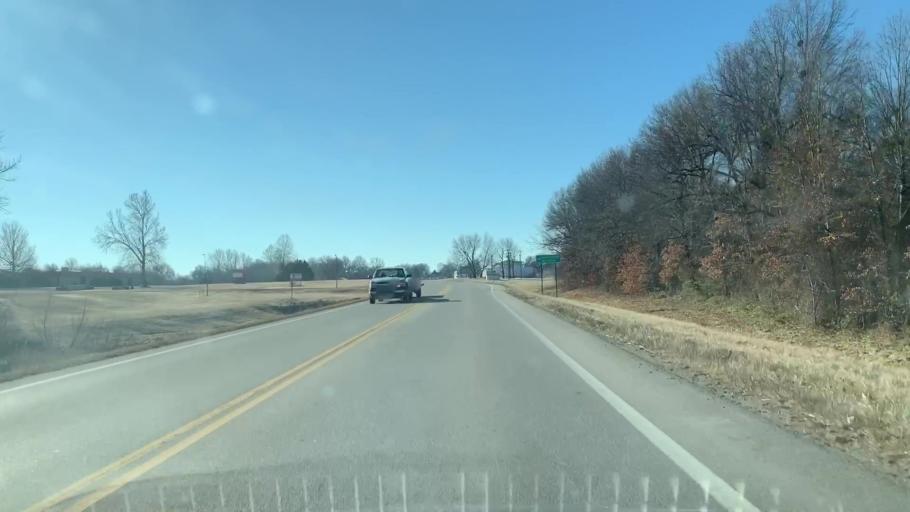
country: US
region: Kansas
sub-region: Cherokee County
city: Baxter Springs
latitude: 37.0390
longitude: -94.7353
